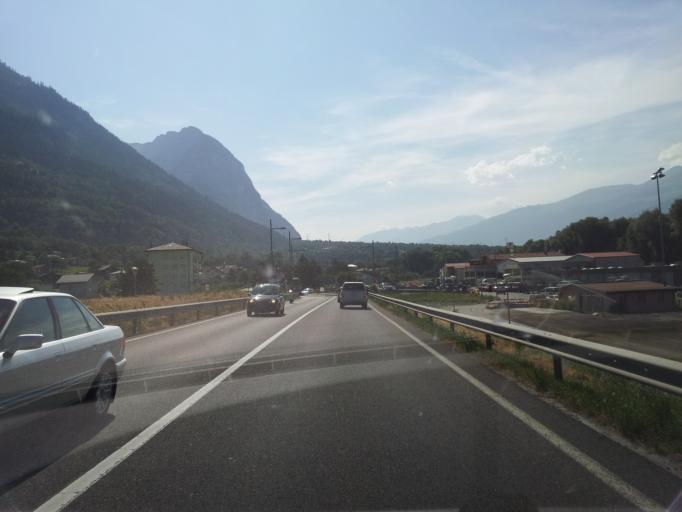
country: CH
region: Valais
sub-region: Leuk District
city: Turtmann
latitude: 46.2982
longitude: 7.6691
